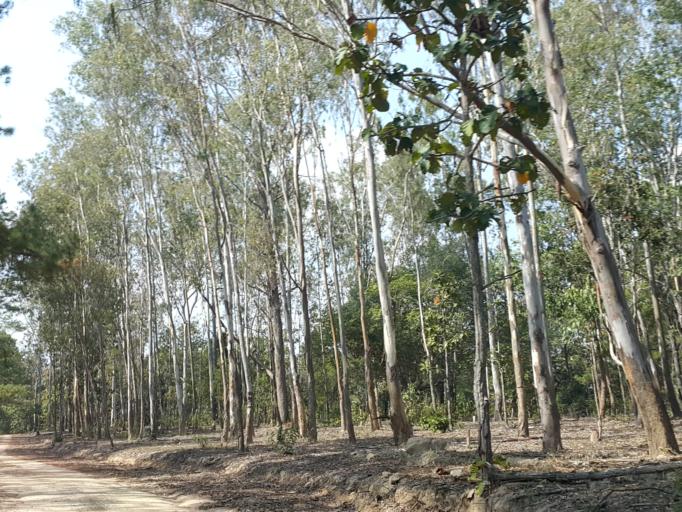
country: TH
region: Chiang Mai
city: Hot
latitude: 18.1522
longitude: 98.4304
